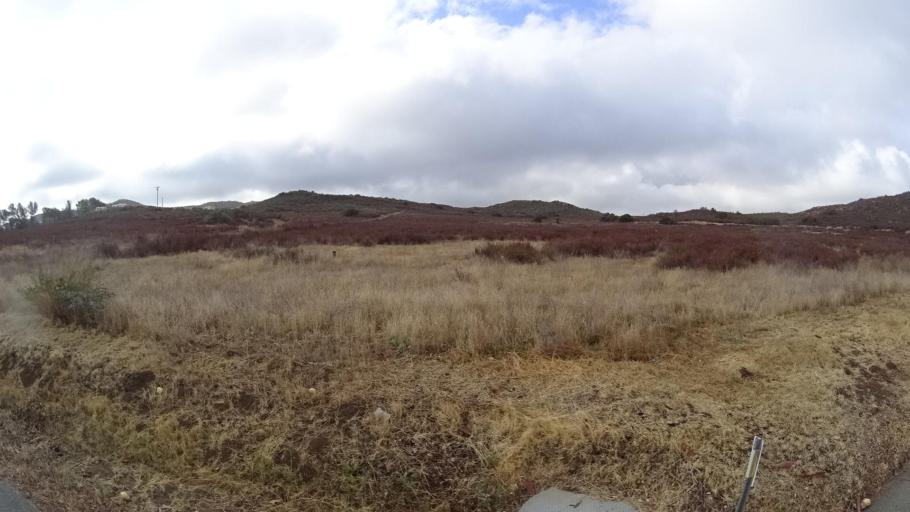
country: MX
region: Baja California
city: Tecate
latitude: 32.6151
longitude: -116.6010
